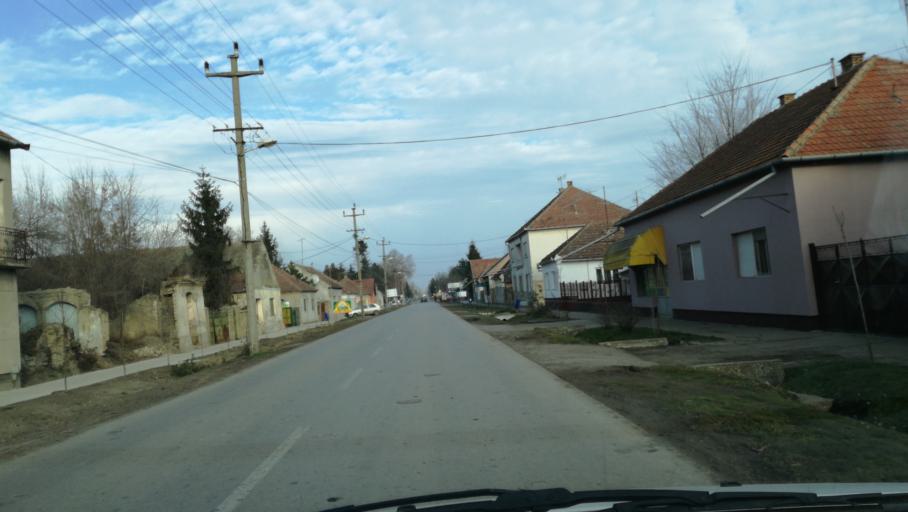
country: RS
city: Rusko Selo
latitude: 45.7568
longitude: 20.5744
